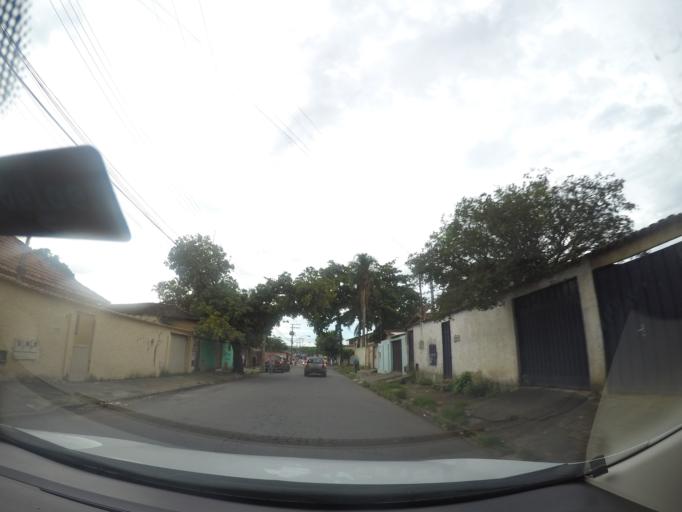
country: BR
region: Goias
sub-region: Goiania
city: Goiania
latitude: -16.6654
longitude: -49.2842
